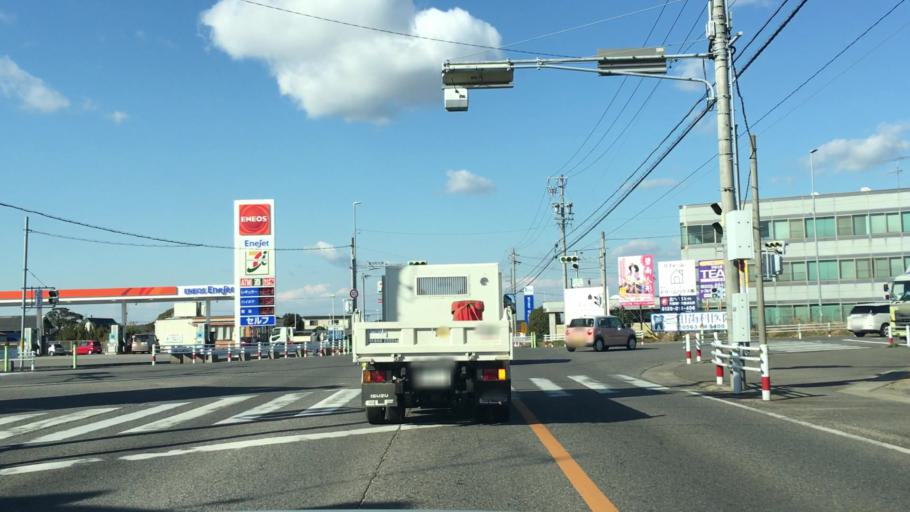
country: JP
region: Aichi
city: Nishio
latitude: 34.8471
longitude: 137.0465
